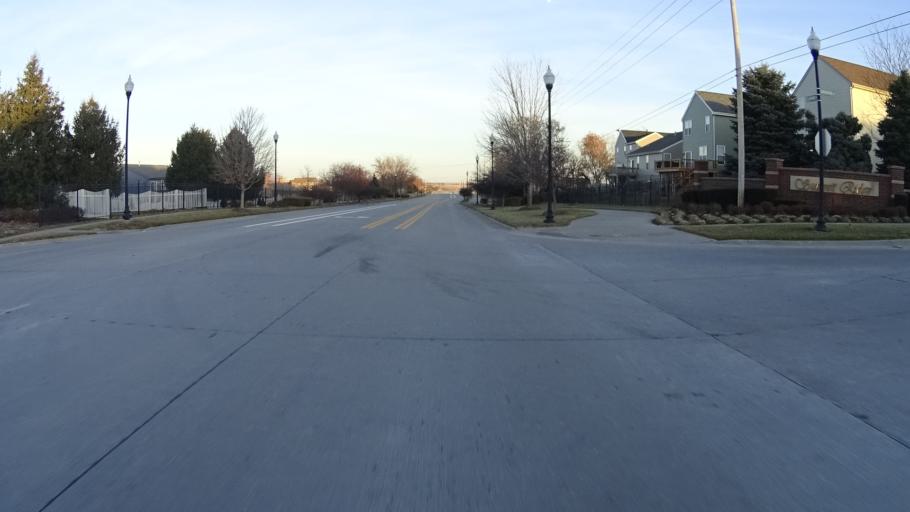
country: US
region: Nebraska
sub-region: Sarpy County
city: Papillion
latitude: 41.1326
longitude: -96.0554
